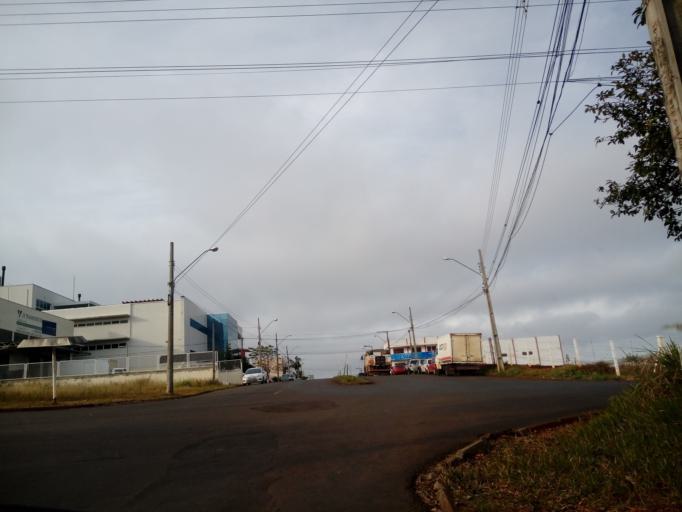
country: BR
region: Santa Catarina
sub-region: Chapeco
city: Chapeco
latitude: -27.0755
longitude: -52.6203
